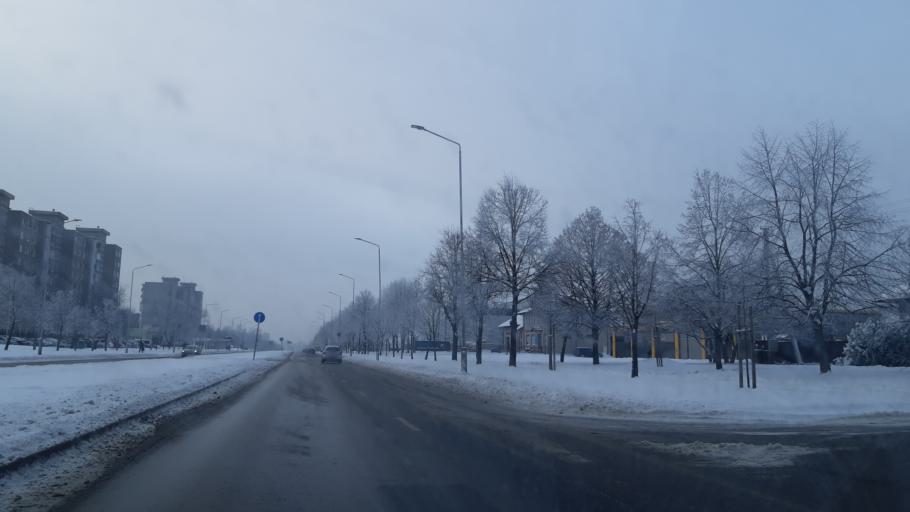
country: LT
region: Kauno apskritis
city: Dainava (Kaunas)
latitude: 54.9309
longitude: 23.9628
